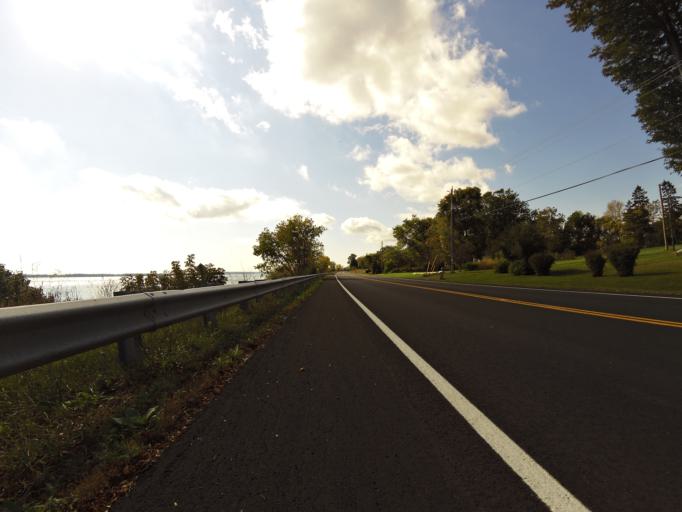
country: CA
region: Ontario
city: Skatepark
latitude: 44.1345
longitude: -76.8618
